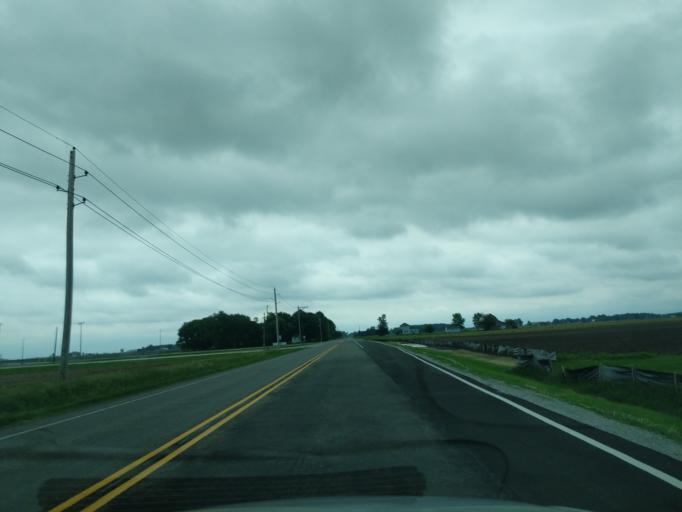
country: US
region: Indiana
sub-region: Tipton County
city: Tipton
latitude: 40.2834
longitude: -86.0060
